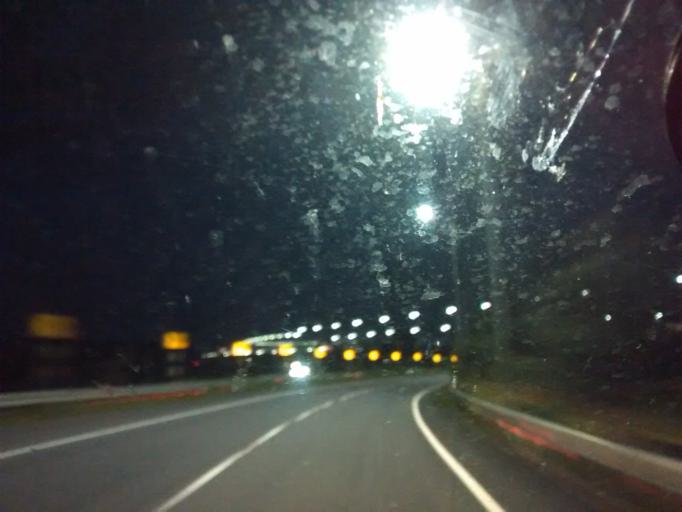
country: IN
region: Telangana
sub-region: Rangareddi
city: Sriramnagar
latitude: 17.2513
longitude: 78.3760
